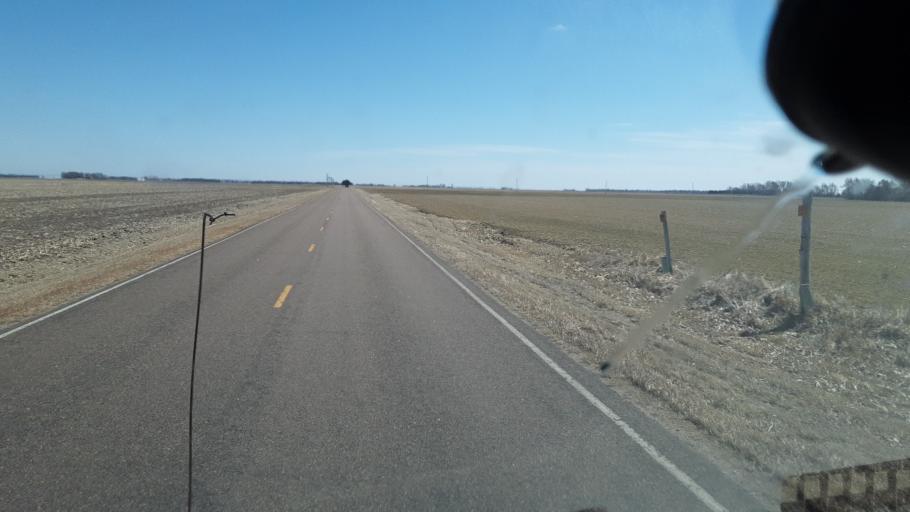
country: US
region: Kansas
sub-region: Rice County
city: Sterling
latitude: 38.2462
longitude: -98.2771
